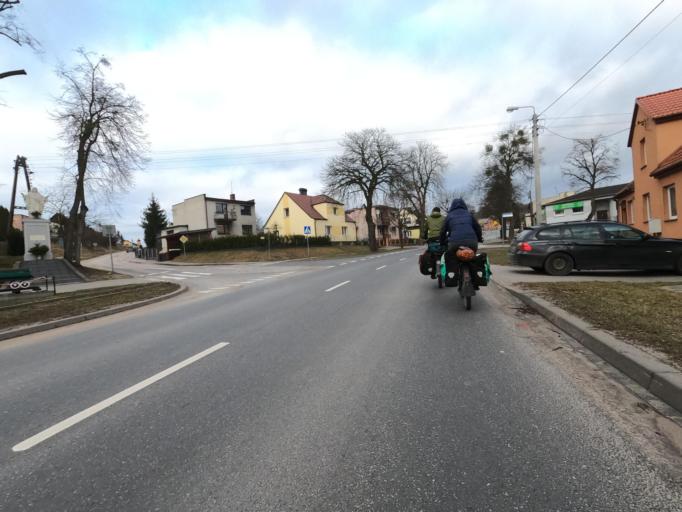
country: PL
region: Greater Poland Voivodeship
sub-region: Powiat pilski
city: Bialosliwie
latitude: 53.0999
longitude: 17.1221
